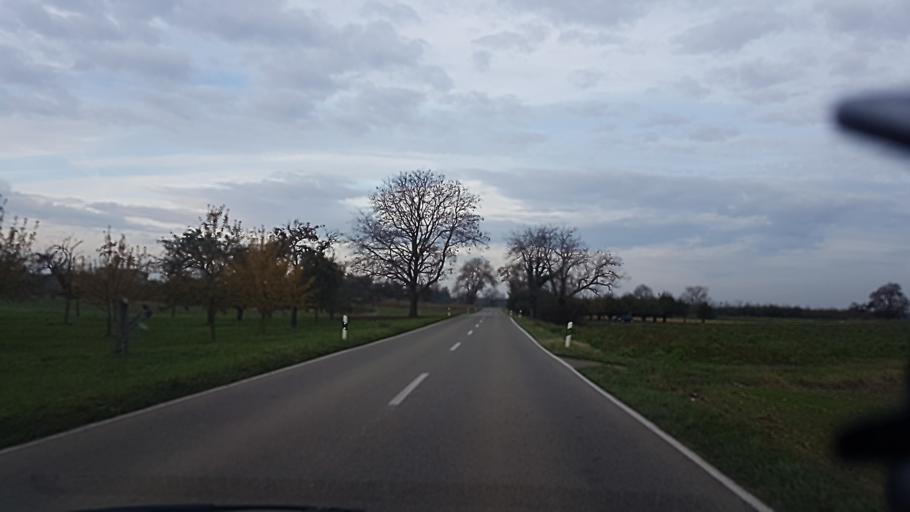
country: DE
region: Baden-Wuerttemberg
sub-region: Freiburg Region
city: Wyhl
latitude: 48.1788
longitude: 7.6641
